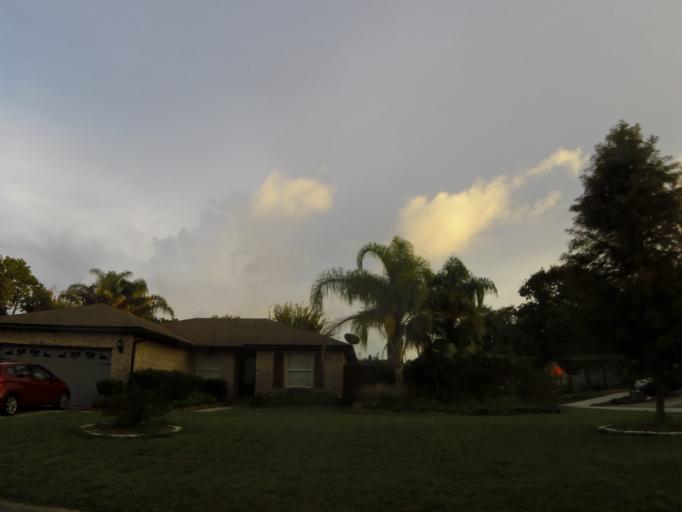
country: US
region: Florida
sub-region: Duval County
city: Atlantic Beach
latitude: 30.3609
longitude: -81.4916
